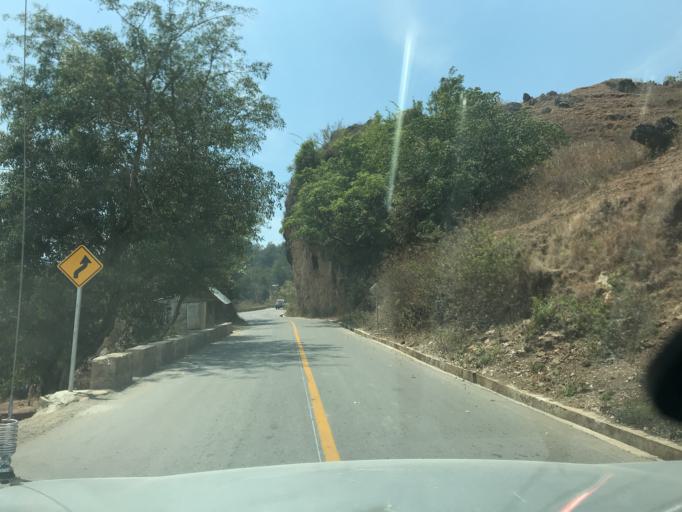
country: TL
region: Aileu
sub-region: Aileu Villa
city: Aileu
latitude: -8.8039
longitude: 125.5914
